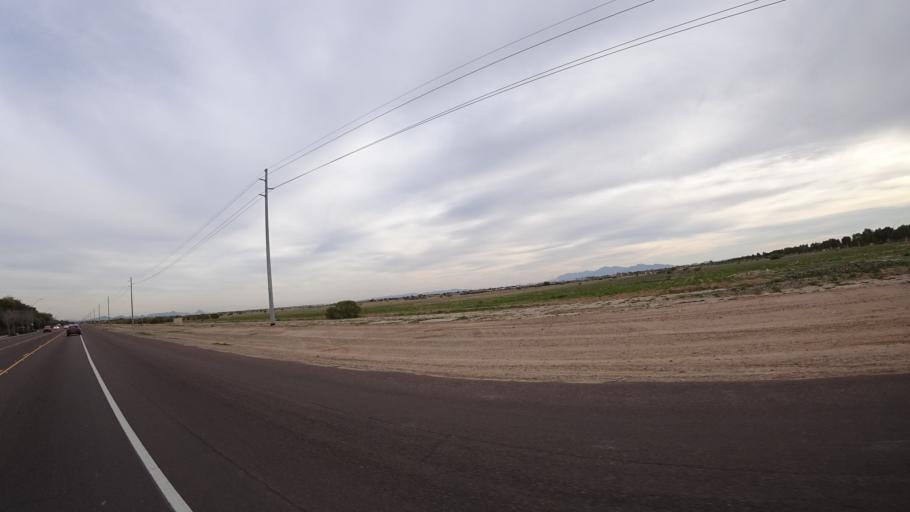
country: US
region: Arizona
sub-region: Maricopa County
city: Surprise
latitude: 33.6093
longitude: -112.3754
